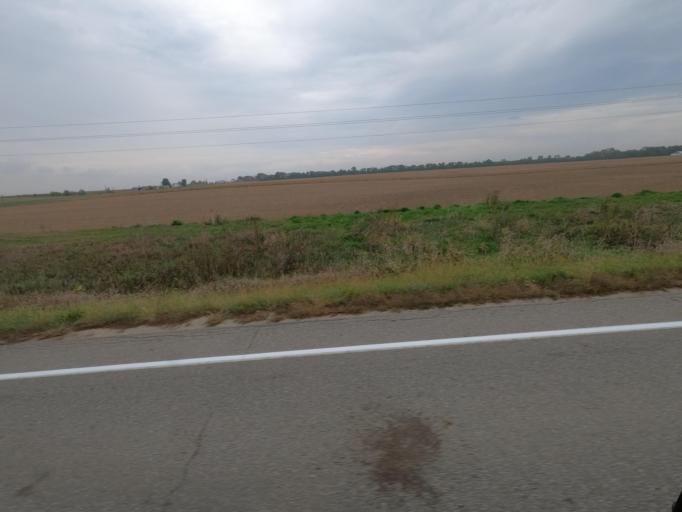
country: US
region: Iowa
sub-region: Van Buren County
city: Keosauqua
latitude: 40.8133
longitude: -91.7734
